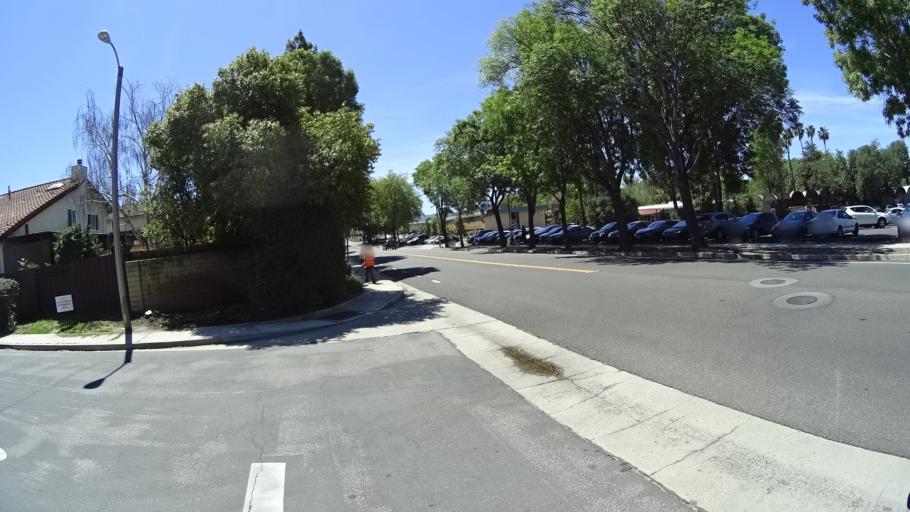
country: US
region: California
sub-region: Ventura County
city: Moorpark
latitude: 34.2244
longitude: -118.8756
